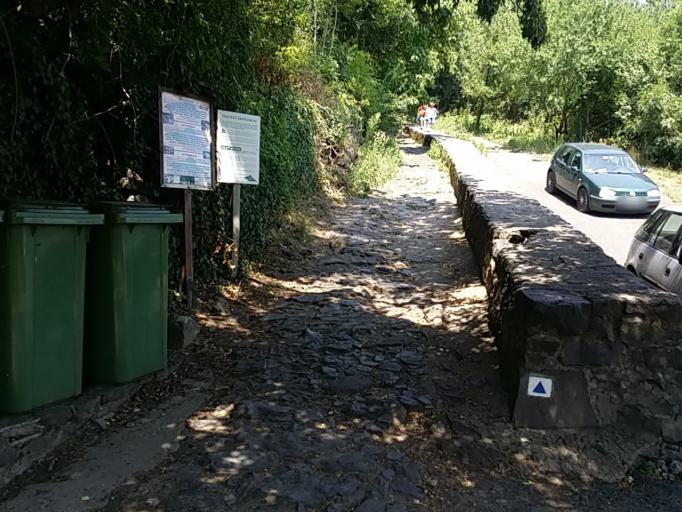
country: HU
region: Veszprem
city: Badacsonytomaj
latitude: 46.7947
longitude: 17.4958
